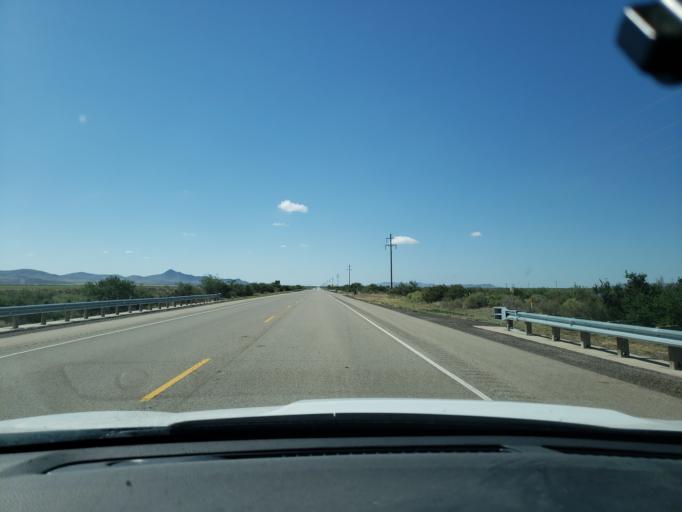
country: US
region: Texas
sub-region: Culberson County
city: Van Horn
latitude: 30.8883
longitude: -104.7914
